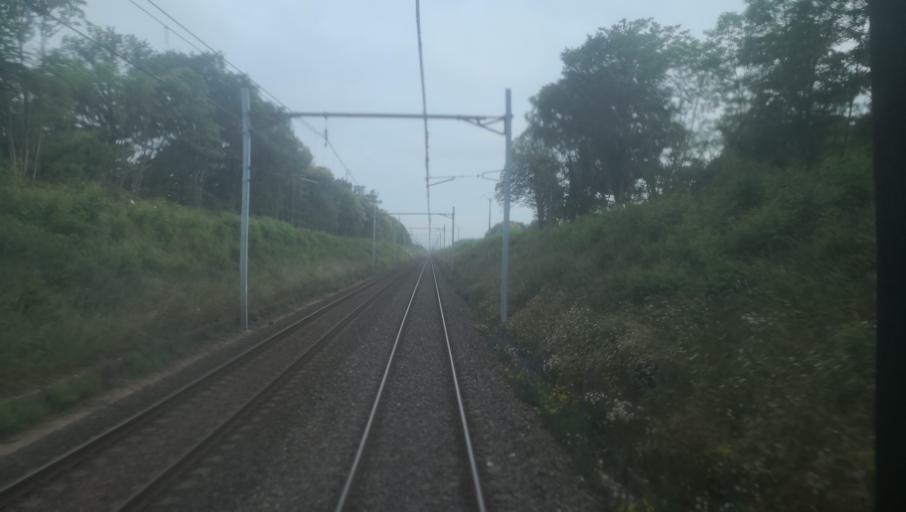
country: FR
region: Centre
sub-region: Departement du Loir-et-Cher
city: Lamotte-Beuvron
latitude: 47.6350
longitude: 1.9964
